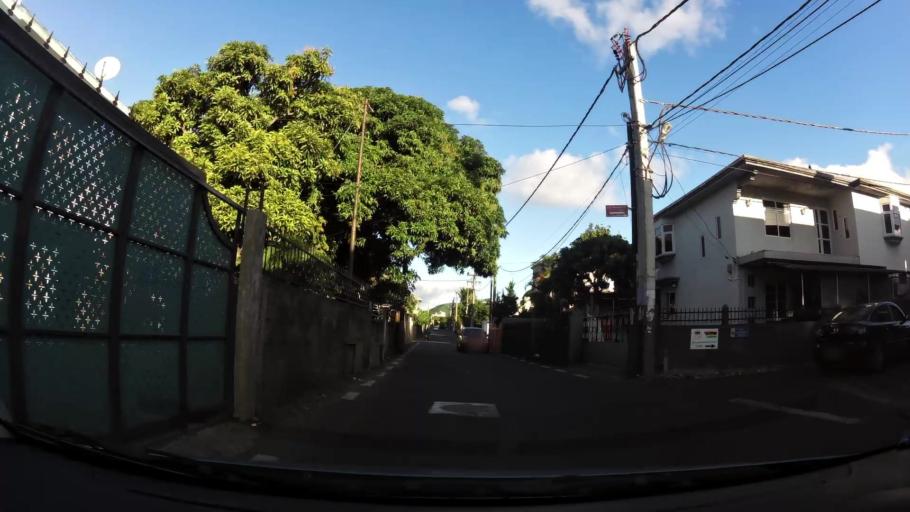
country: MU
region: Plaines Wilhems
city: Quatre Bornes
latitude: -20.2512
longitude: 57.4706
